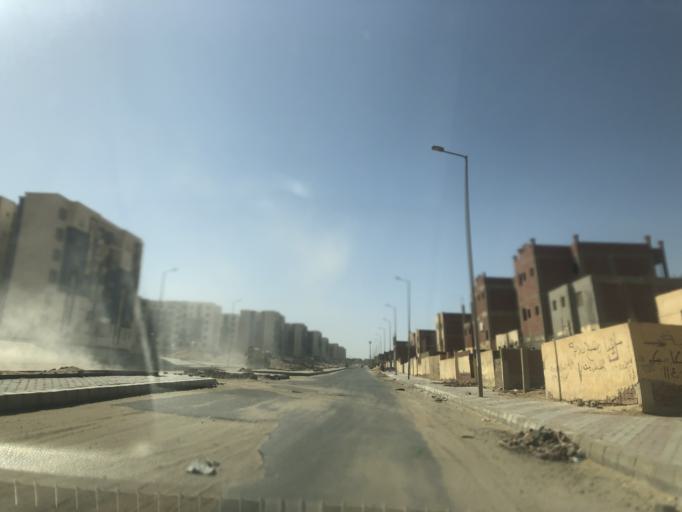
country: EG
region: Al Jizah
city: Madinat Sittah Uktubar
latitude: 29.9311
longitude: 30.9872
